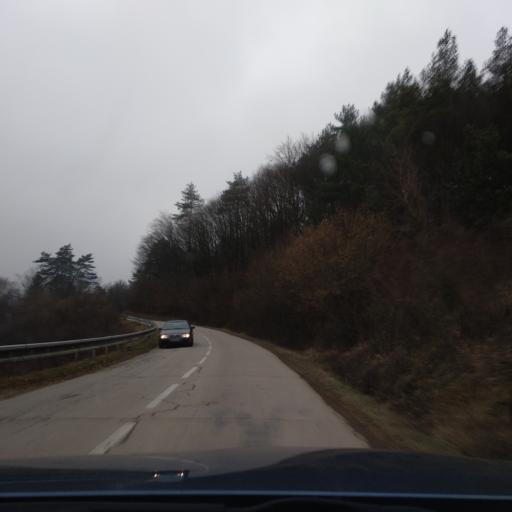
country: SK
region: Nitriansky
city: Trencianske Teplice
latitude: 48.9025
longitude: 18.2544
